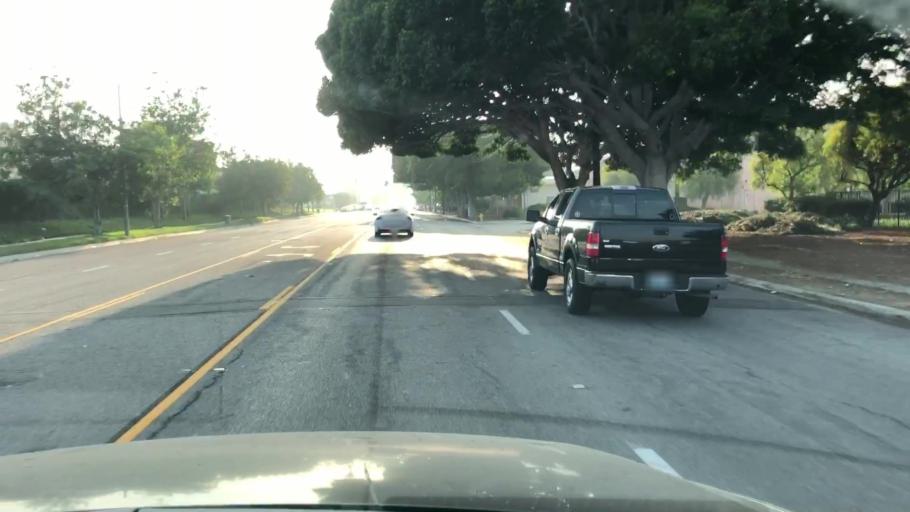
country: US
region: California
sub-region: Ventura County
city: Port Hueneme
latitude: 34.1548
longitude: -119.1818
